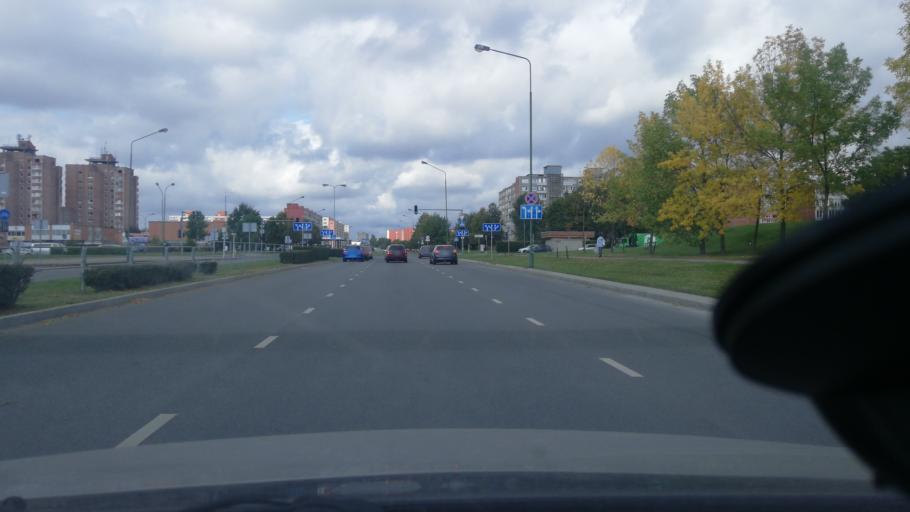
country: LT
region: Klaipedos apskritis
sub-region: Klaipeda
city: Klaipeda
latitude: 55.6697
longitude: 21.1940
